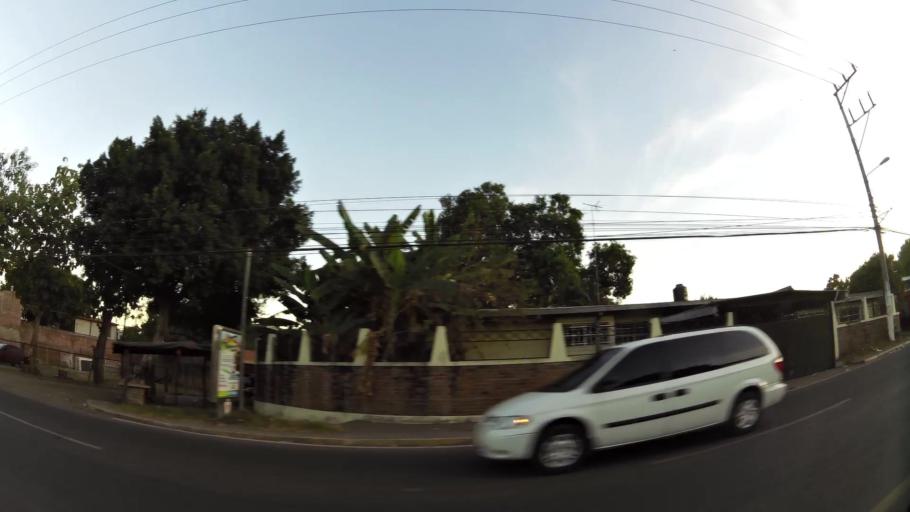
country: SV
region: San Miguel
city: San Miguel
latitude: 13.4929
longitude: -88.1768
